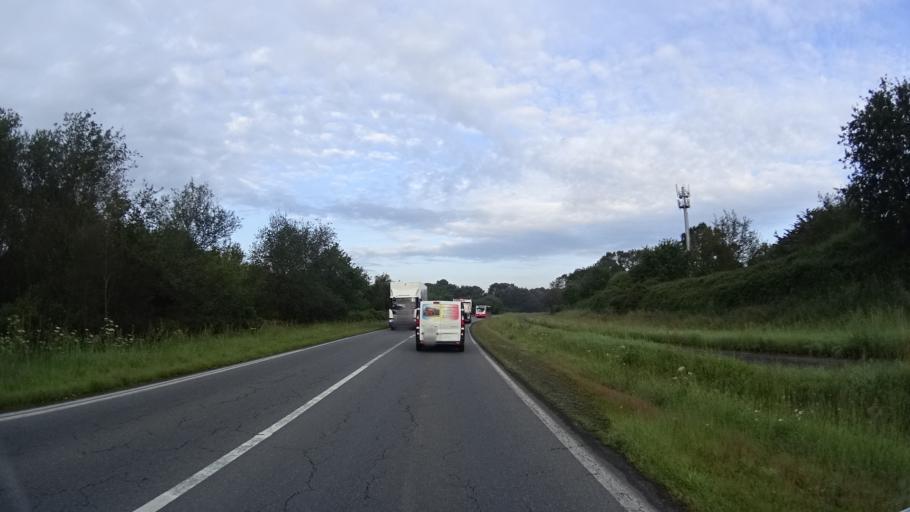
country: FR
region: Brittany
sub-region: Departement du Morbihan
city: Sene
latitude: 47.6422
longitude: -2.7319
